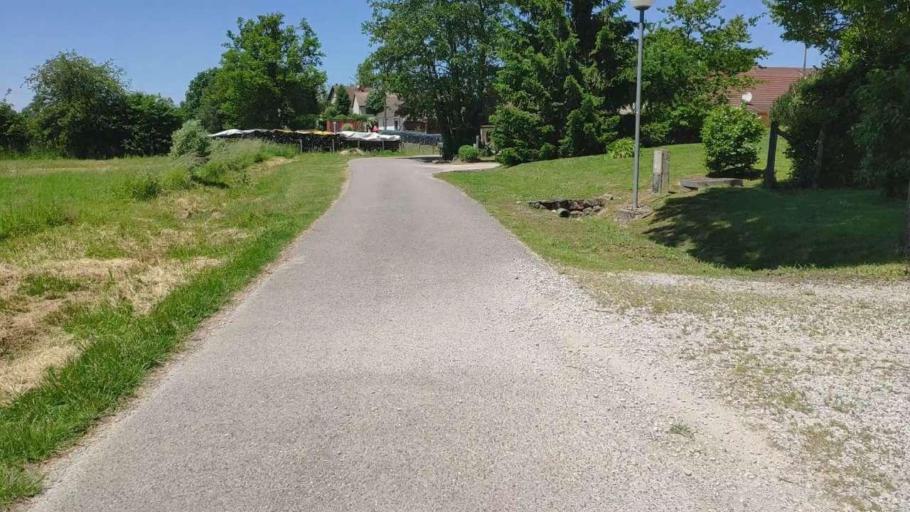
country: FR
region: Franche-Comte
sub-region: Departement du Jura
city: Bletterans
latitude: 46.7400
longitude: 5.4218
